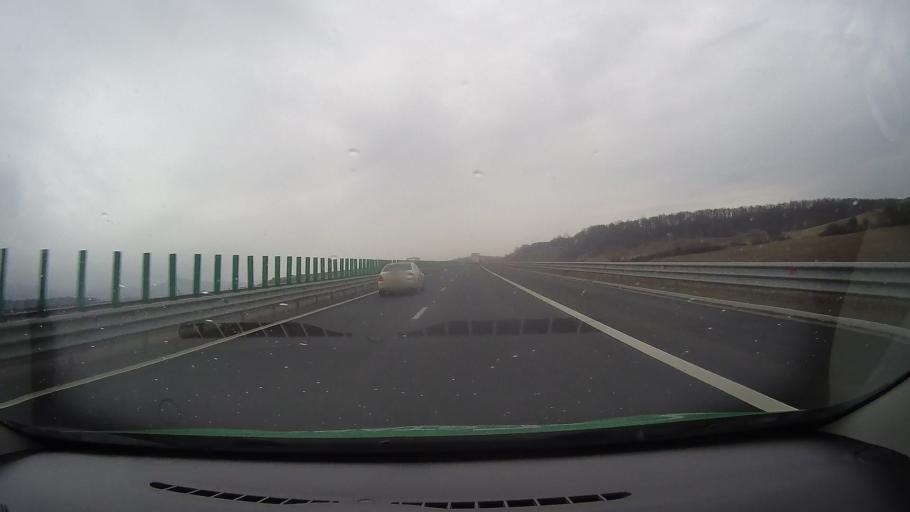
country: RO
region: Alba
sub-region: Comuna Blandiana
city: Blandiana
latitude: 45.9531
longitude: 23.4306
